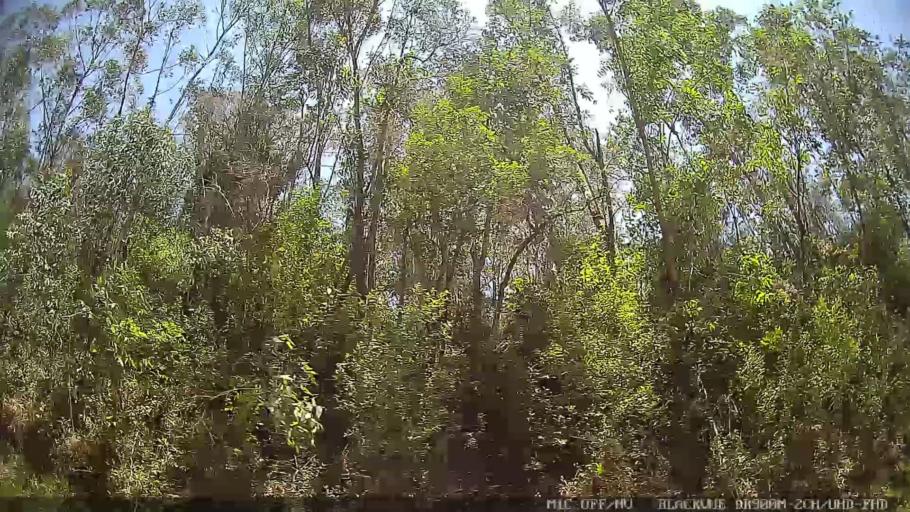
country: BR
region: Sao Paulo
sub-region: Francisco Morato
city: Francisco Morato
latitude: -23.2897
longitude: -46.7886
